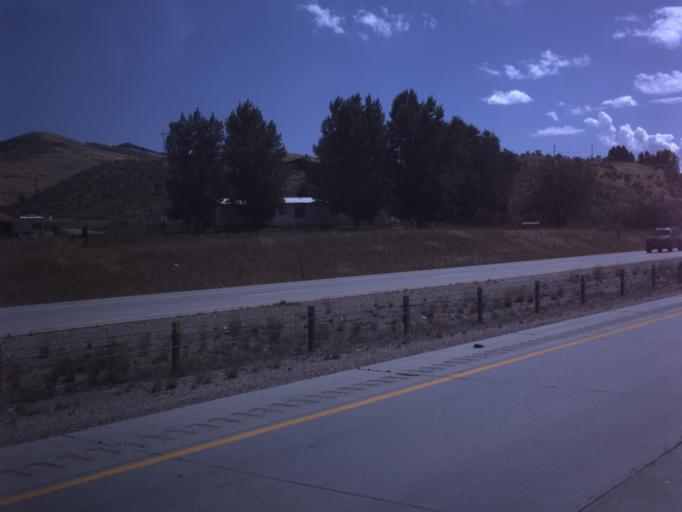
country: US
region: Utah
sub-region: Morgan County
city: Mountain Green
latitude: 41.0895
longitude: -111.7357
